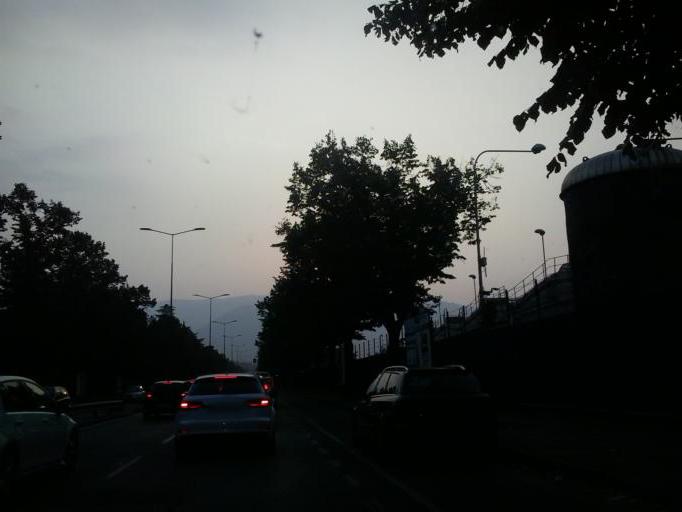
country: IT
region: Lombardy
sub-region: Provincia di Brescia
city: Collebeato
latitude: 45.5600
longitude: 10.2151
